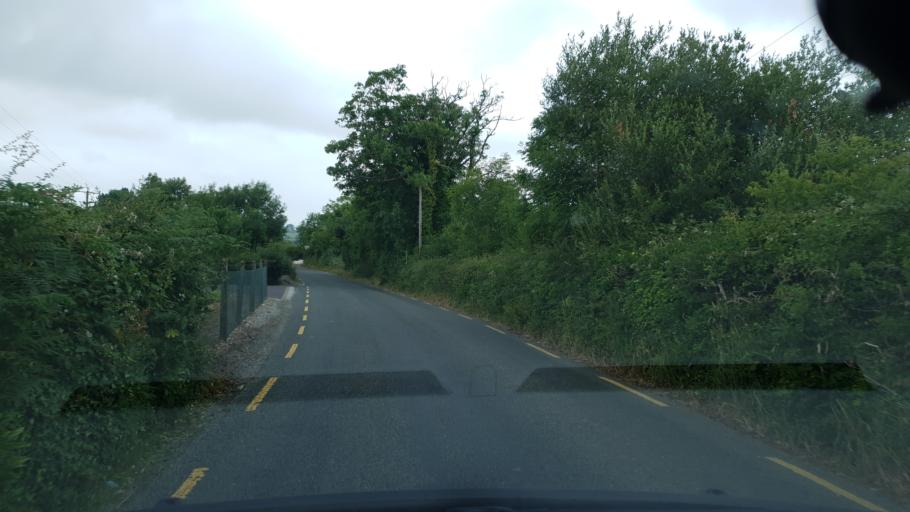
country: IE
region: Munster
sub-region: Ciarrai
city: Cill Airne
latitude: 52.1361
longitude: -9.5546
